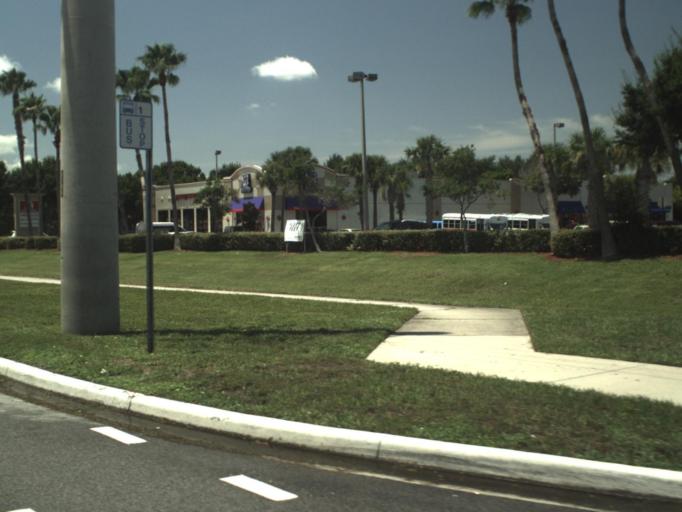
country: US
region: Florida
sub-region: Martin County
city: North River Shores
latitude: 27.2357
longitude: -80.2688
